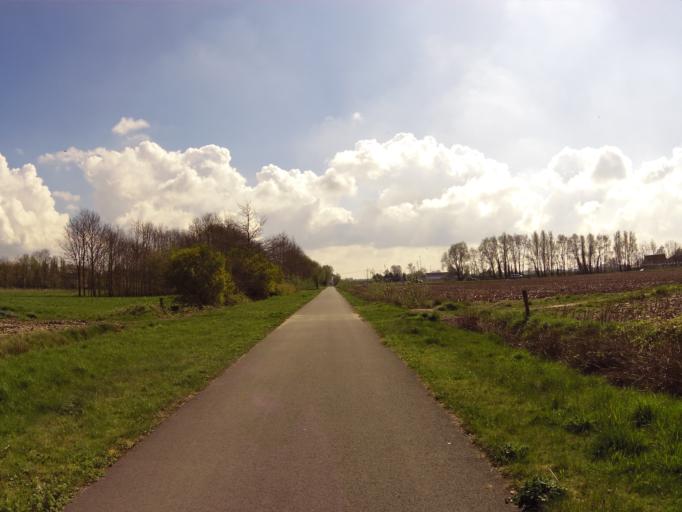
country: BE
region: Flanders
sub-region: Provincie West-Vlaanderen
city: Ichtegem
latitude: 51.1225
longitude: 3.0262
